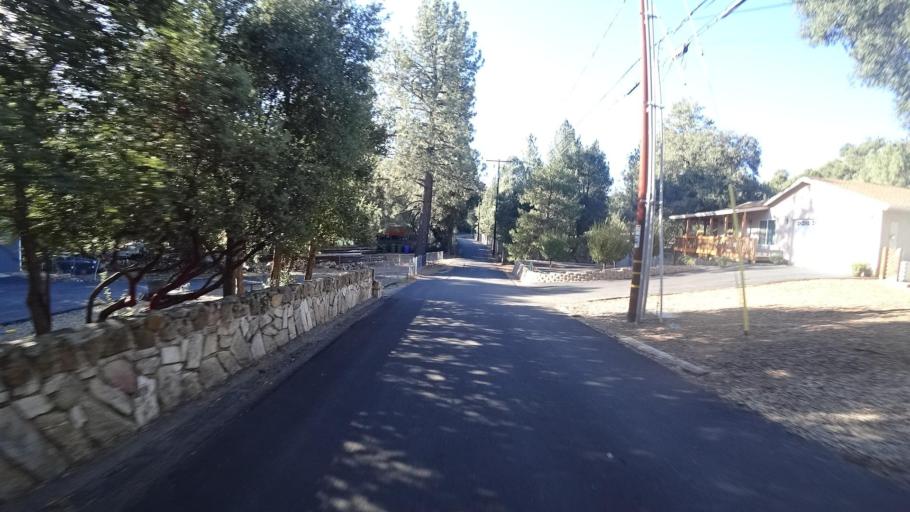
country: US
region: California
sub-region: San Diego County
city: Pine Valley
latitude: 32.8257
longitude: -116.5349
